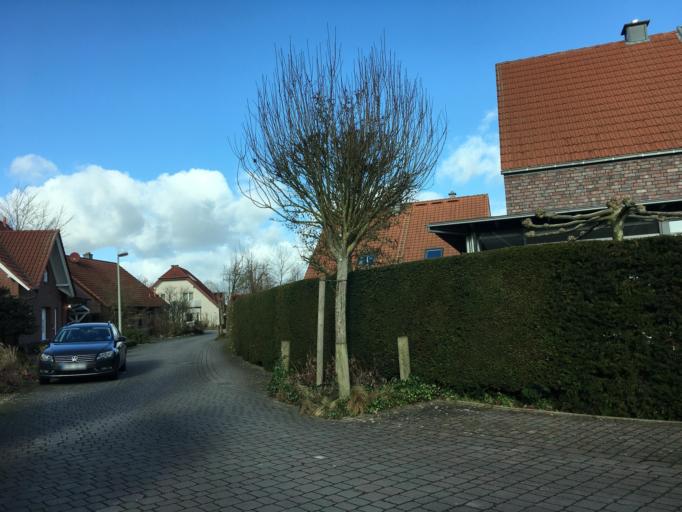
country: DE
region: North Rhine-Westphalia
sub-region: Regierungsbezirk Munster
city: Havixbeck
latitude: 51.9717
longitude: 7.4248
